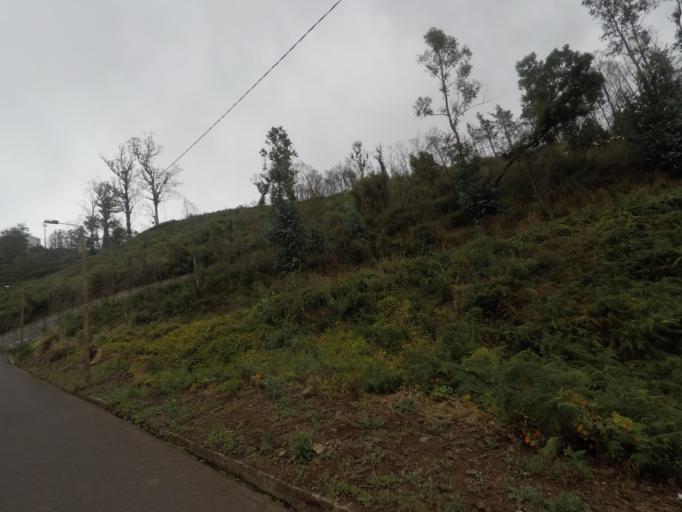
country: PT
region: Madeira
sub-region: Funchal
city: Nossa Senhora do Monte
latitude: 32.6677
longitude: -16.8879
